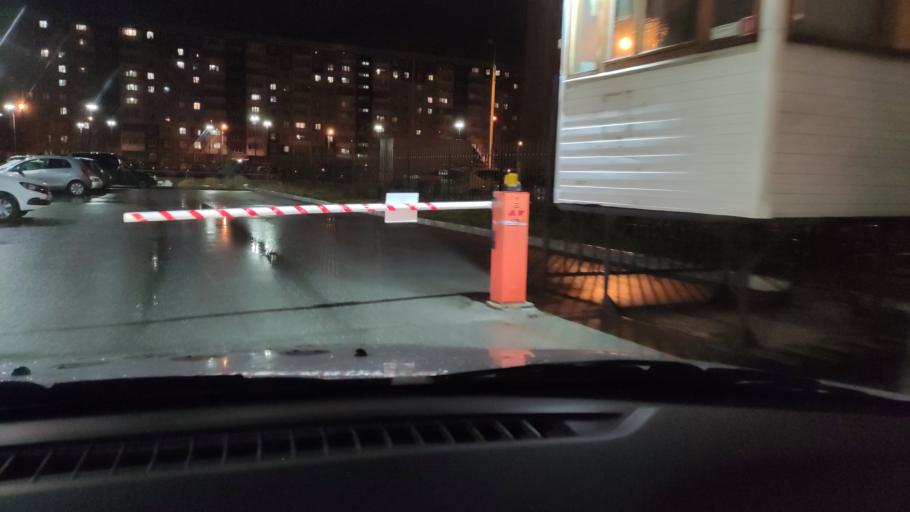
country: RU
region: Perm
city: Kondratovo
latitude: 57.9992
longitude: 56.1394
